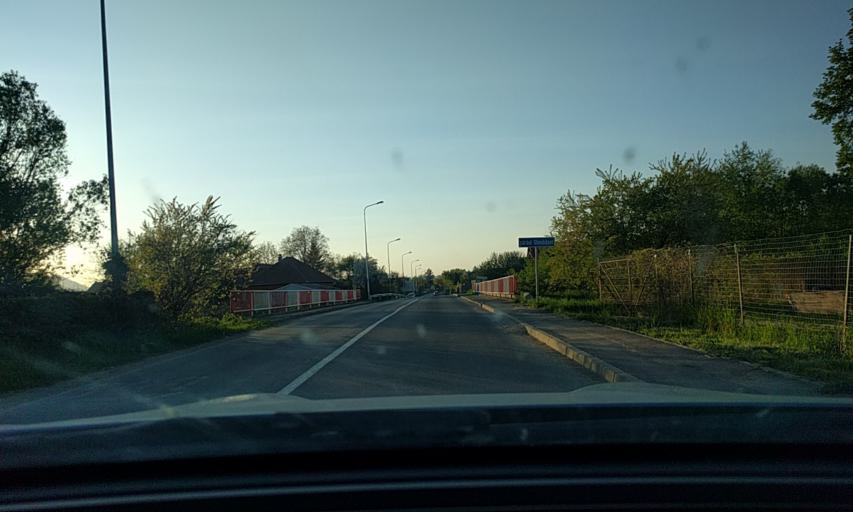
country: RO
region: Brasov
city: Brasov
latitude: 45.6912
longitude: 25.5654
